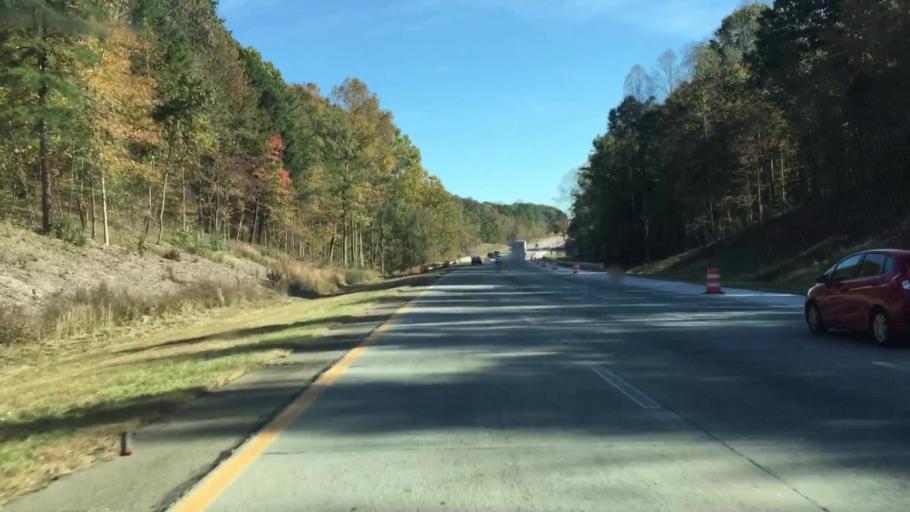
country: US
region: North Carolina
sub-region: Davidson County
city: Thomasville
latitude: 35.8292
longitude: -80.1591
